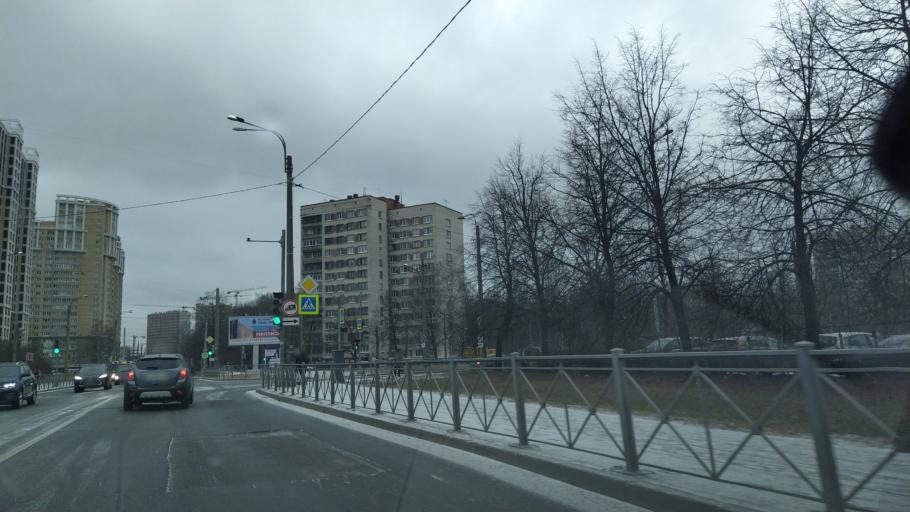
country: RU
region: St.-Petersburg
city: Kupchino
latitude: 59.8414
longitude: 30.3162
